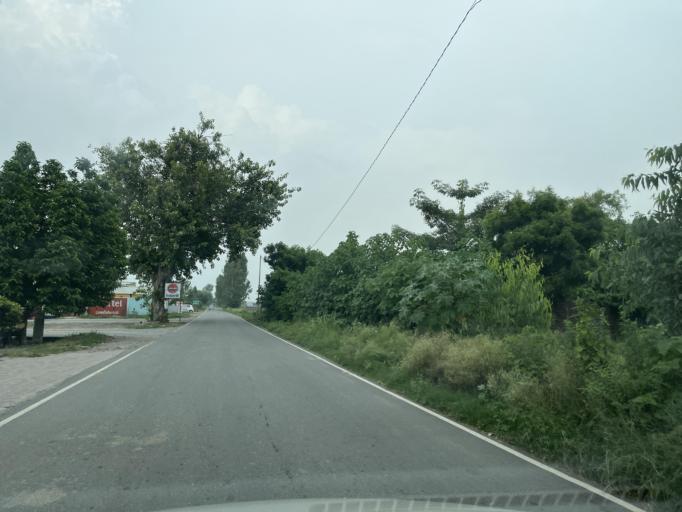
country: IN
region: Uttarakhand
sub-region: Naini Tal
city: Haldwani
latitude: 29.1746
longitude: 79.4699
